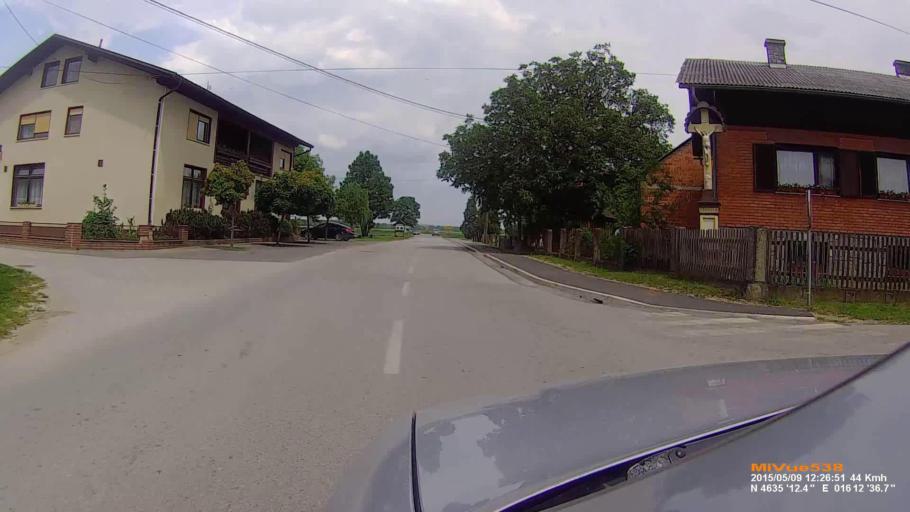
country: SI
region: Beltinci
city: Beltinci
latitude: 46.5868
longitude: 16.2102
